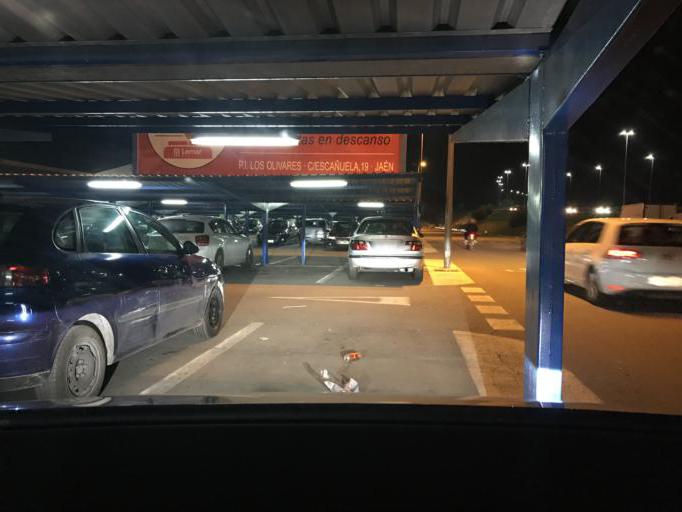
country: ES
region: Andalusia
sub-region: Provincia de Jaen
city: Jaen
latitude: 37.7815
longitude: -3.7652
